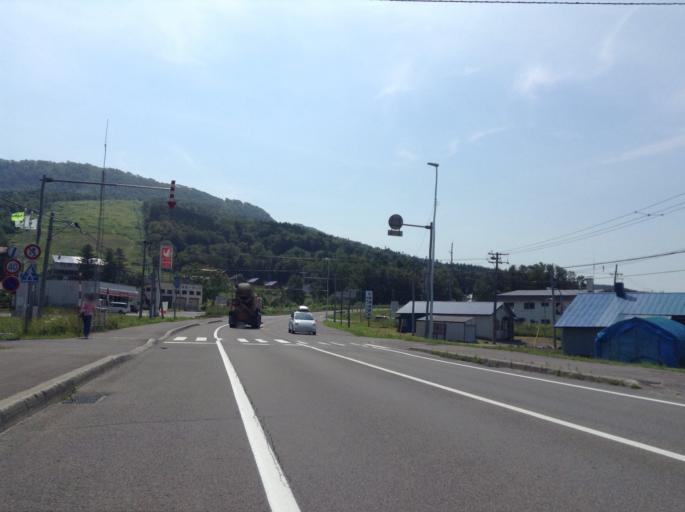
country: JP
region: Hokkaido
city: Nayoro
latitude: 44.7236
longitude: 142.2675
